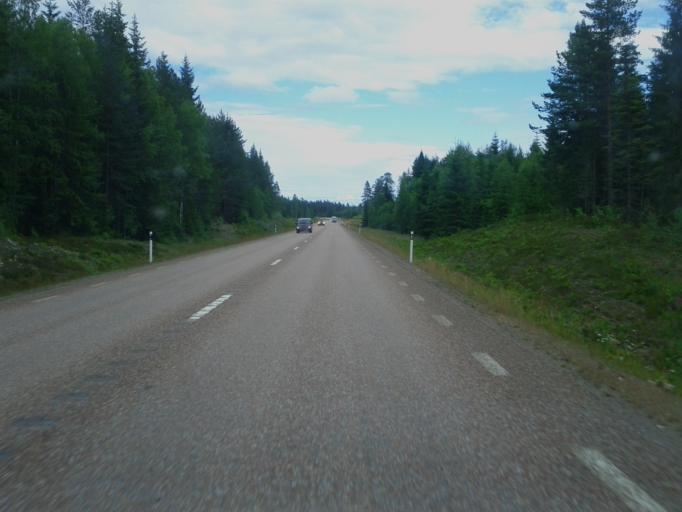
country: SE
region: Dalarna
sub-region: Faluns Kommun
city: Bjursas
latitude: 60.7487
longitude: 15.3579
